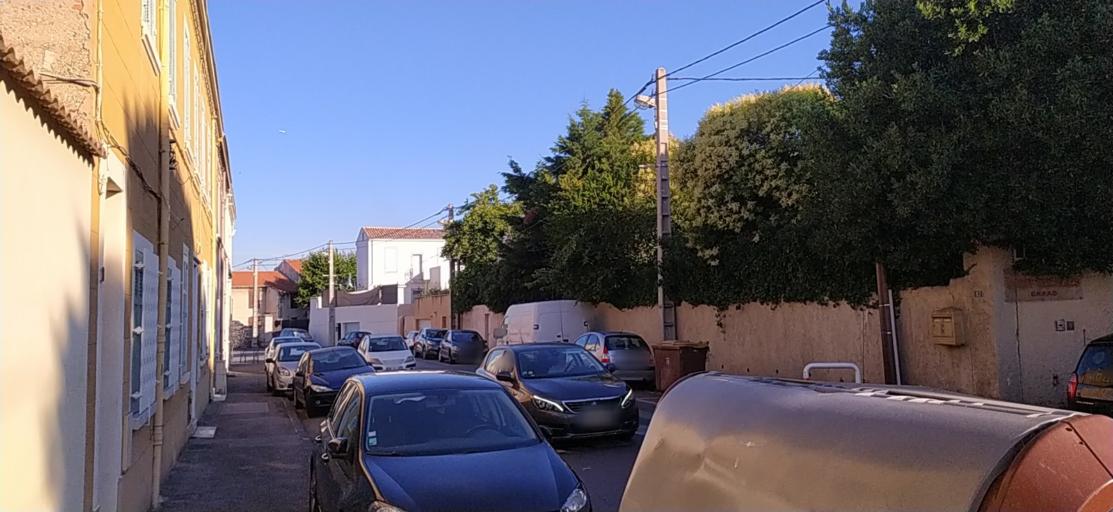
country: FR
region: Provence-Alpes-Cote d'Azur
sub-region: Departement des Bouches-du-Rhone
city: Marseille 16
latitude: 43.3576
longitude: 5.3399
